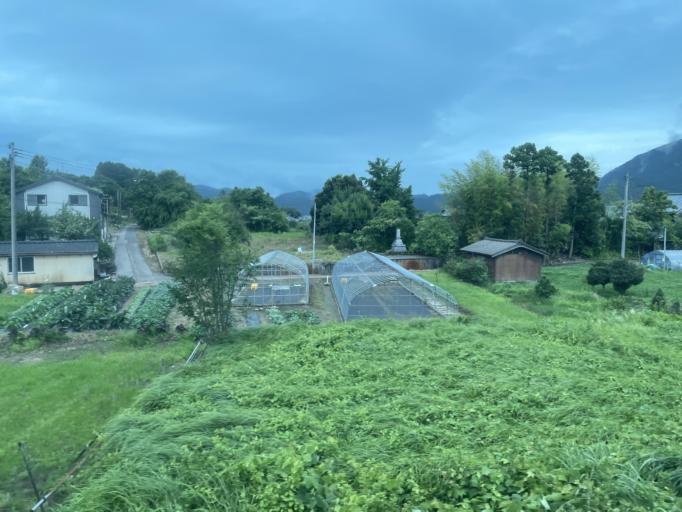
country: JP
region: Niigata
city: Yoshida-kasugacho
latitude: 37.6967
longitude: 138.8472
